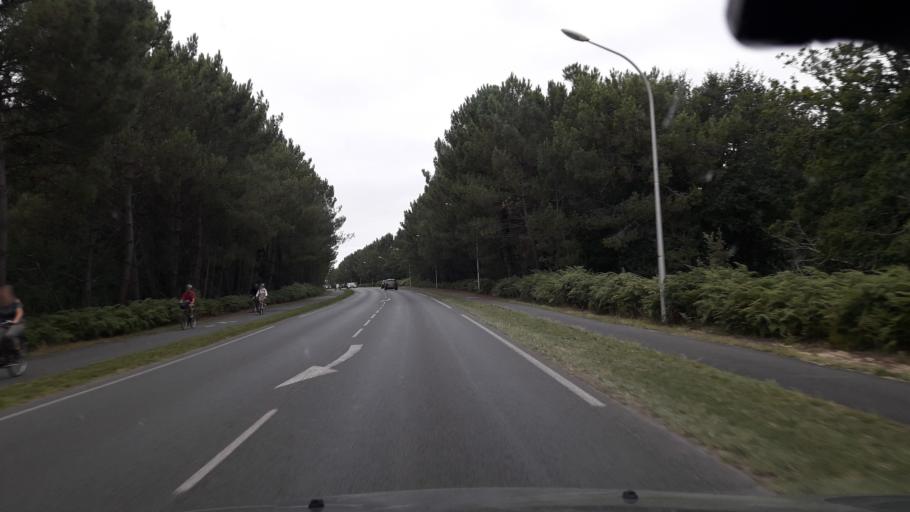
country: FR
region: Poitou-Charentes
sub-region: Departement de la Charente-Maritime
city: Les Mathes
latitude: 45.7077
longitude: -1.1618
